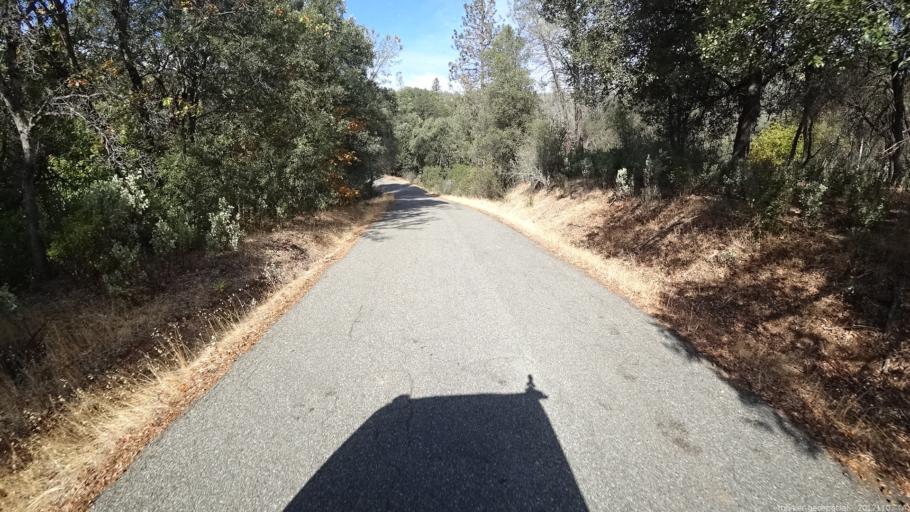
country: US
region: California
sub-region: Shasta County
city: Shasta
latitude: 40.5329
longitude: -122.5563
